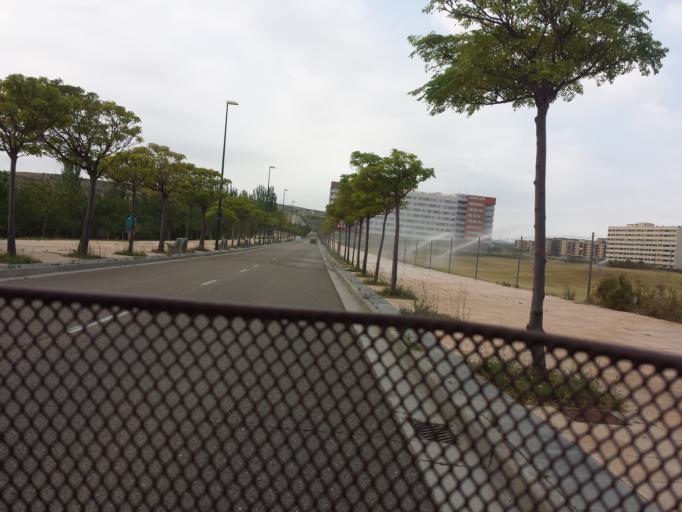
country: ES
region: Aragon
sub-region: Provincia de Zaragoza
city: Montecanal
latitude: 41.6240
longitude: -0.9425
